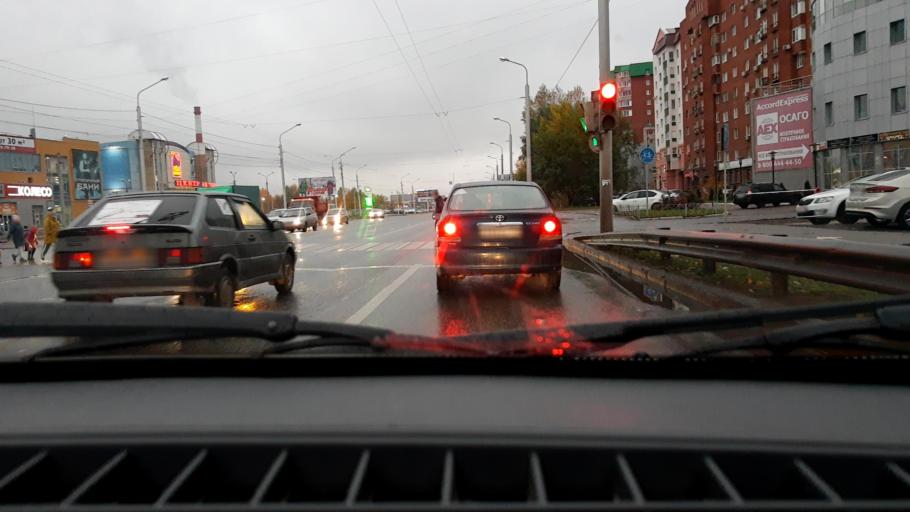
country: RU
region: Bashkortostan
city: Ufa
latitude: 54.7776
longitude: 56.0690
